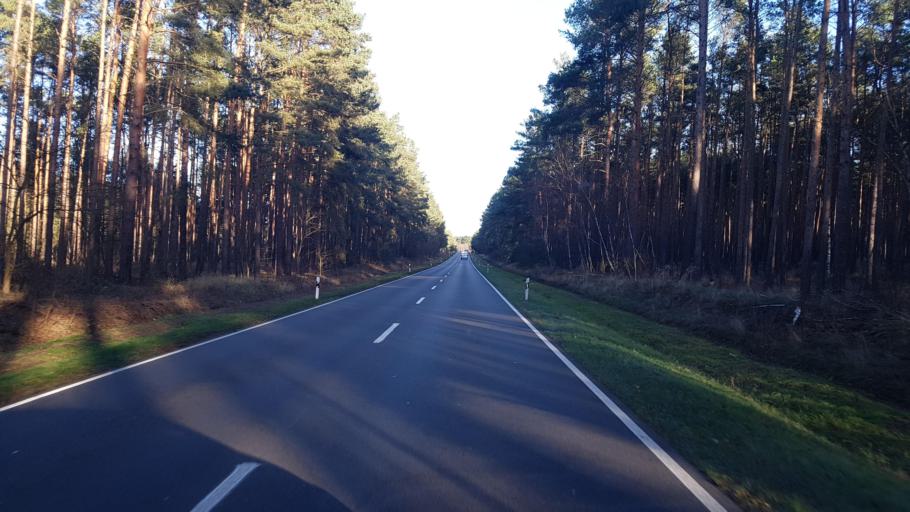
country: DE
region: Brandenburg
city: Heinersbruck
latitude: 51.7215
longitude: 14.4585
